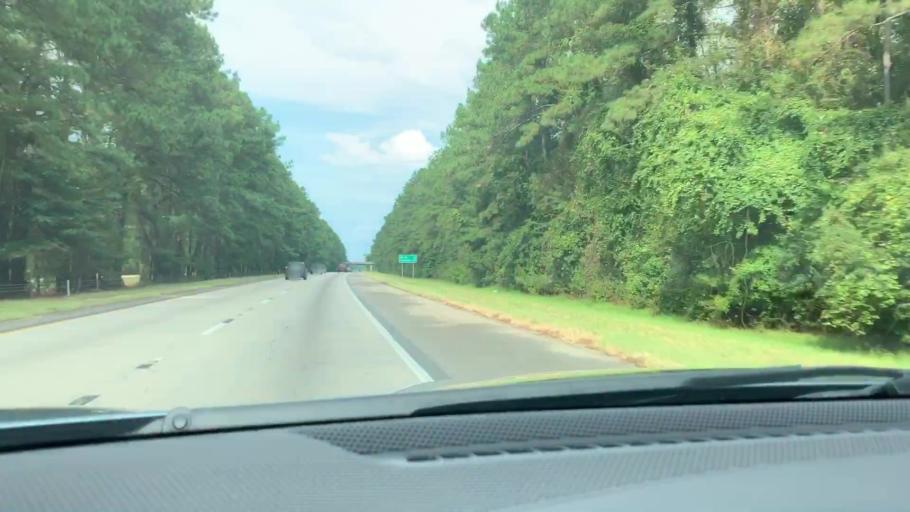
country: US
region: South Carolina
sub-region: Colleton County
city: Walterboro
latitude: 32.8912
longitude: -80.7118
